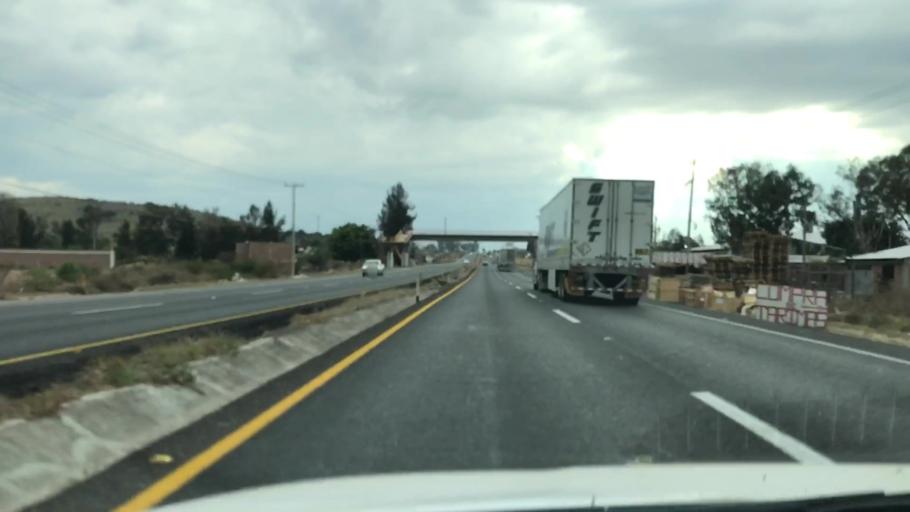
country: MX
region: Guanajuato
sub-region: Irapuato
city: Colonia Morelos de Guadalupe de Rivera
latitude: 20.5739
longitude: -101.4405
